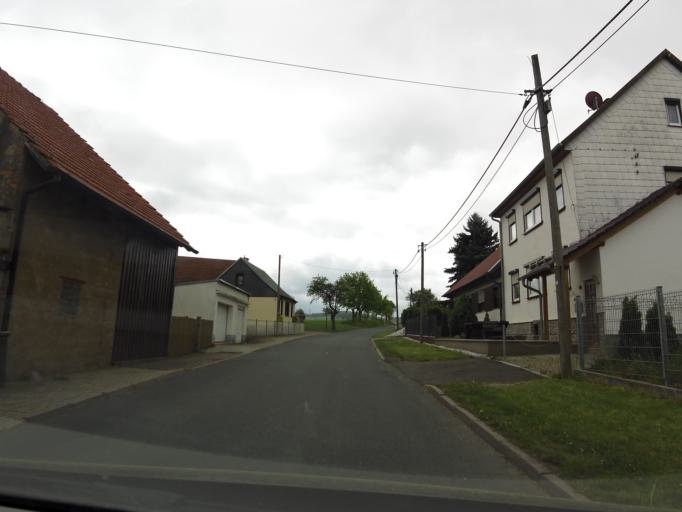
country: DE
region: Thuringia
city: Ernstroda
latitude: 50.8788
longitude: 10.6157
